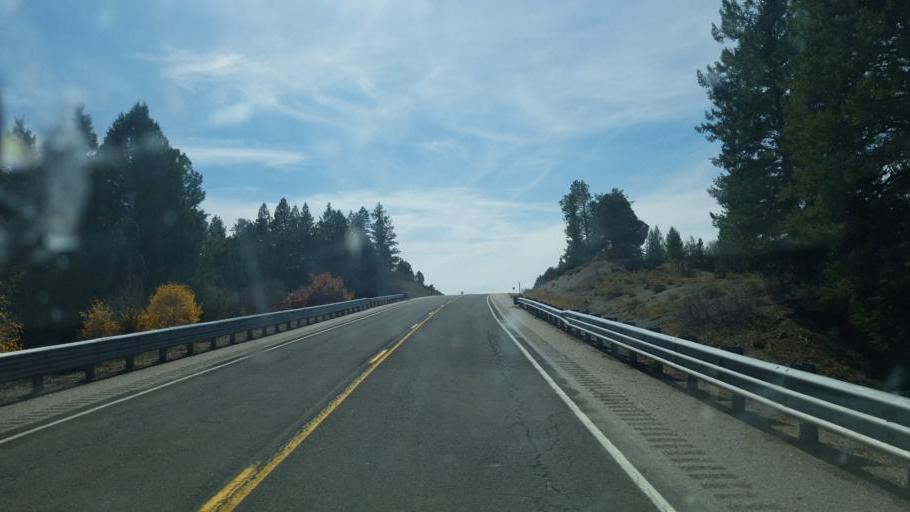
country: US
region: New Mexico
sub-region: Rio Arriba County
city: Chama
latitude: 36.9840
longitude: -106.7804
